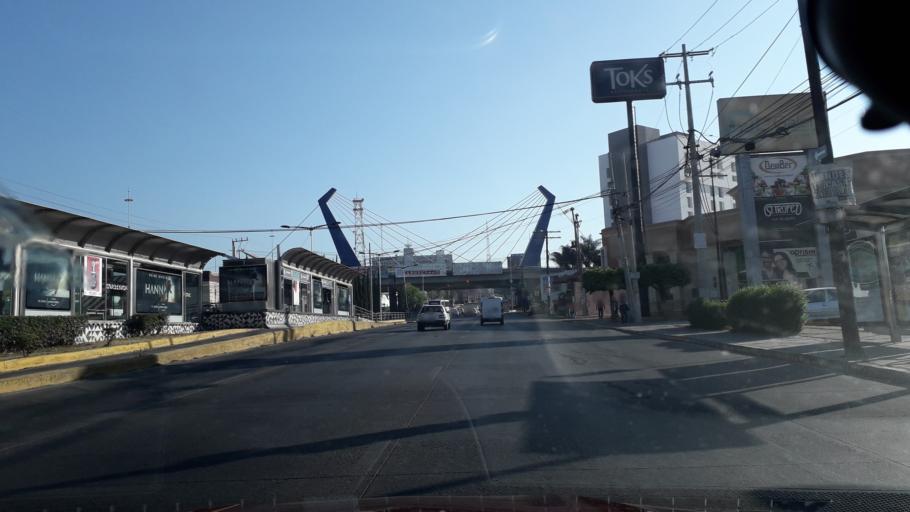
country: MX
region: Puebla
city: Puebla
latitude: 19.0452
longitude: -98.2350
